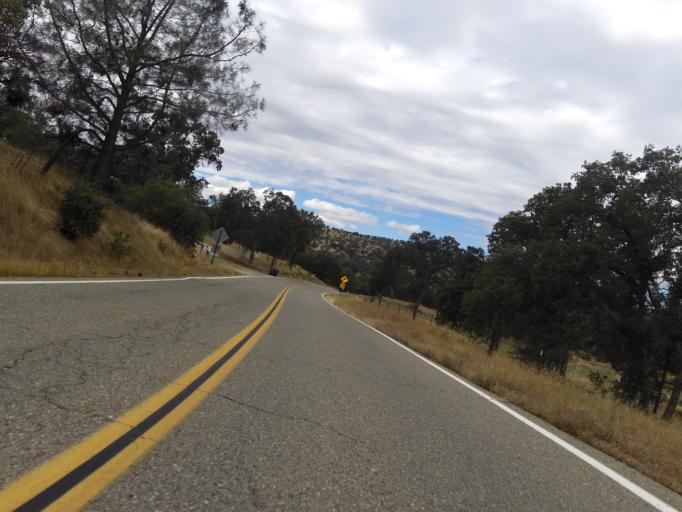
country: US
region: California
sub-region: Madera County
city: Yosemite Lakes
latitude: 37.2352
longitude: -119.7706
